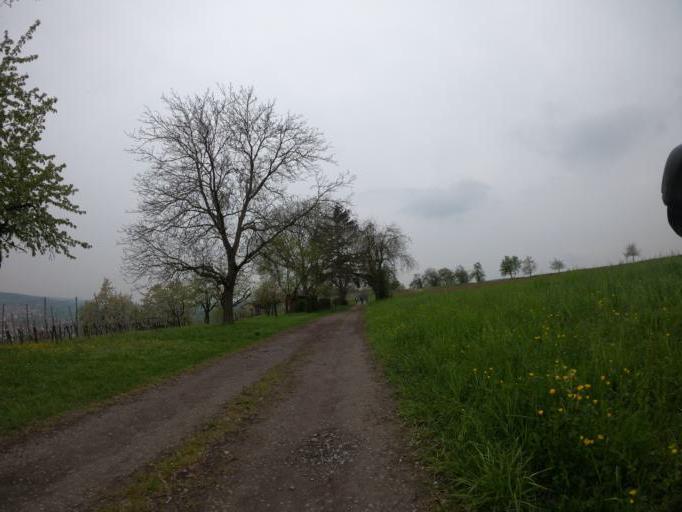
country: DE
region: Baden-Wuerttemberg
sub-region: Regierungsbezirk Stuttgart
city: Oberriexingen
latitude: 48.9447
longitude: 9.0627
